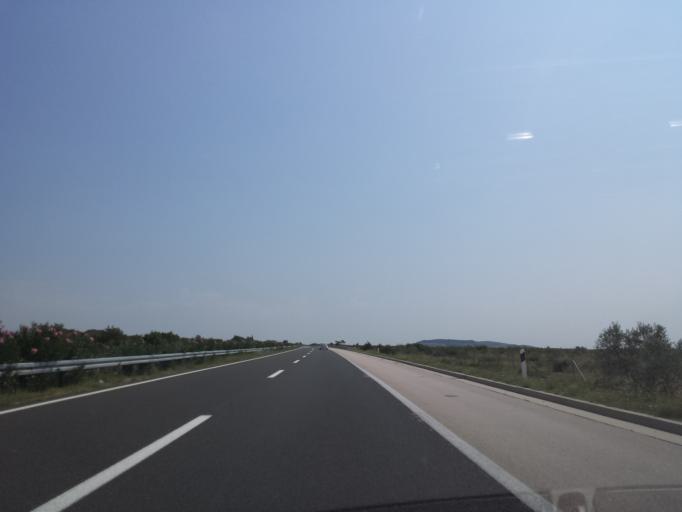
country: HR
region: Zadarska
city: Galovac
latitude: 44.0985
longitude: 15.4713
